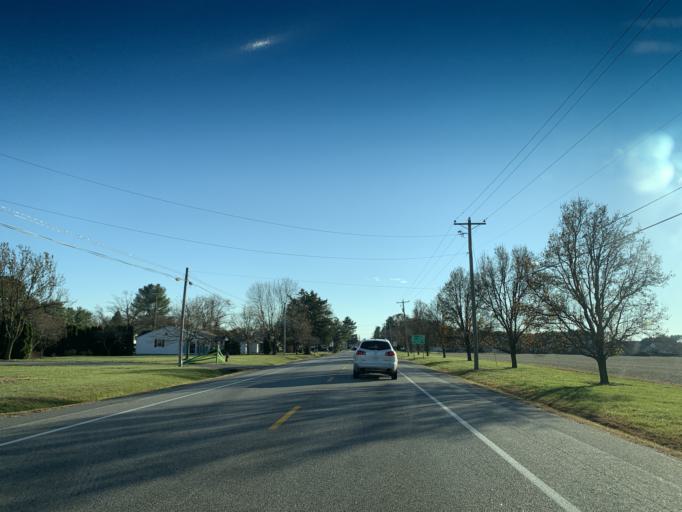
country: US
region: Delaware
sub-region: New Castle County
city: Middletown
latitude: 39.3497
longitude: -75.8781
